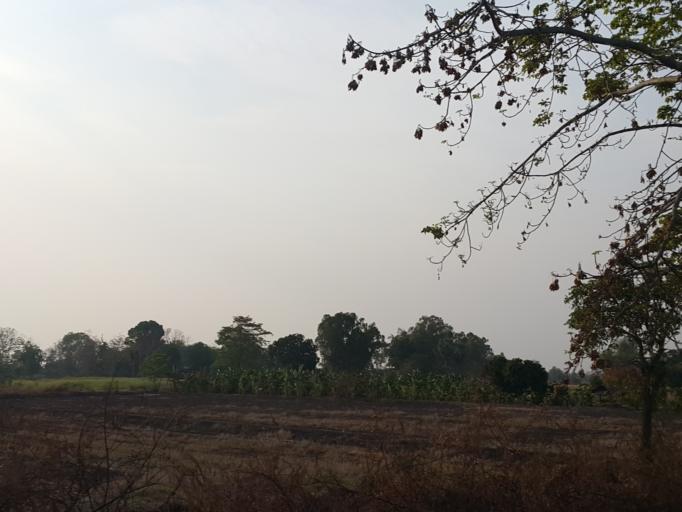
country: TH
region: Sukhothai
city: Si Samrong
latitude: 17.2120
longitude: 99.9487
